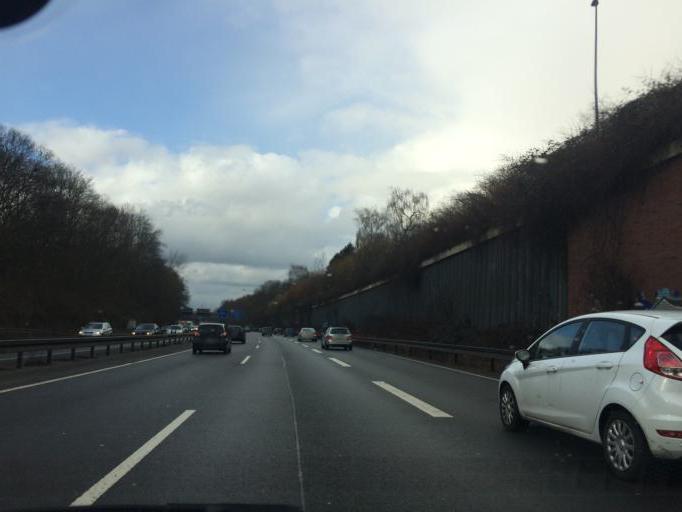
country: DE
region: North Rhine-Westphalia
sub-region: Regierungsbezirk Arnsberg
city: Herne
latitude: 51.5374
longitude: 7.2062
